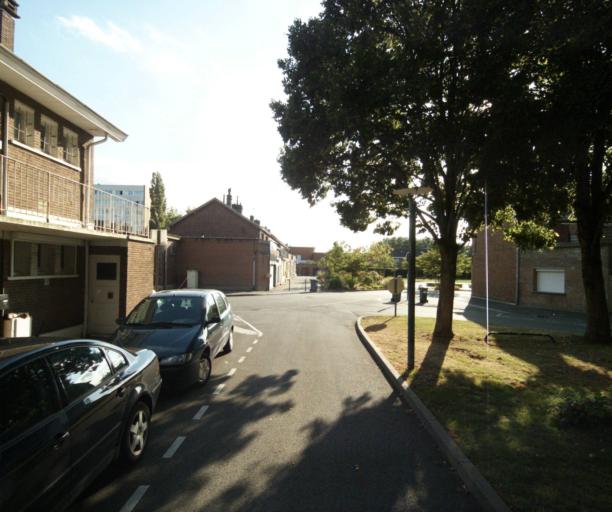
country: FR
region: Nord-Pas-de-Calais
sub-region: Departement du Nord
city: Ronchin
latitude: 50.6199
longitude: 3.0869
